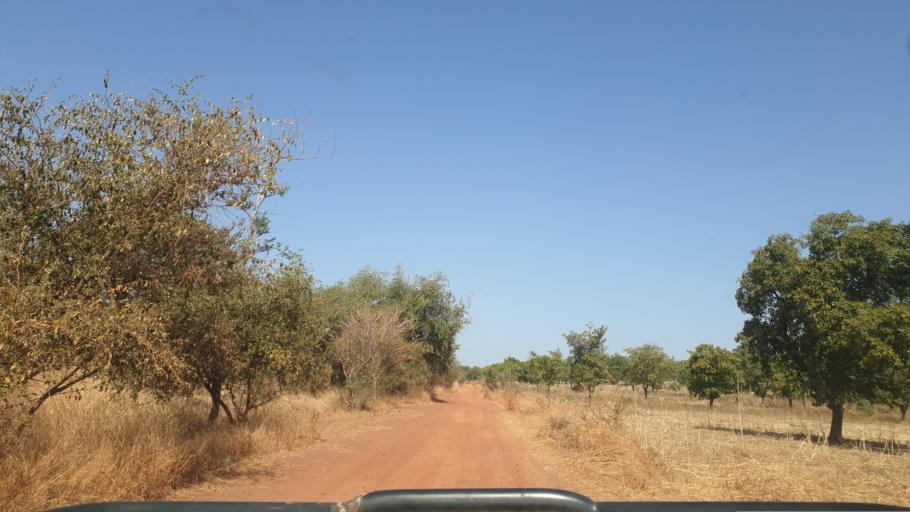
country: ML
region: Koulikoro
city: Dioila
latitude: 11.9062
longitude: -6.9830
